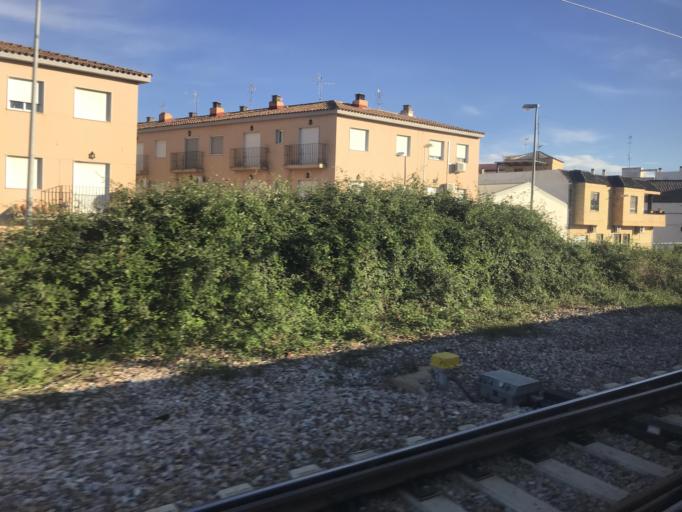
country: ES
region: Valencia
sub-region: Provincia de Valencia
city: Pucol
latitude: 39.6193
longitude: -0.3036
